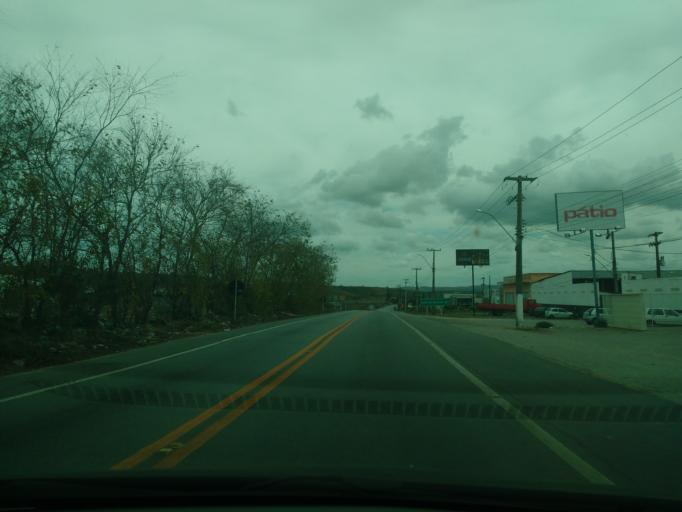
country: BR
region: Alagoas
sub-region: Uniao Dos Palmares
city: Uniao dos Palmares
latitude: -9.1683
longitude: -36.0226
